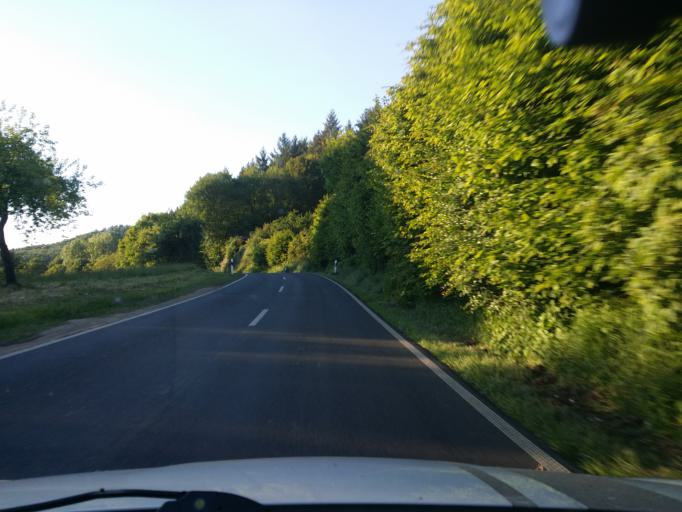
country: DE
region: Hesse
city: Eppstein
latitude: 50.1798
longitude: 8.3669
